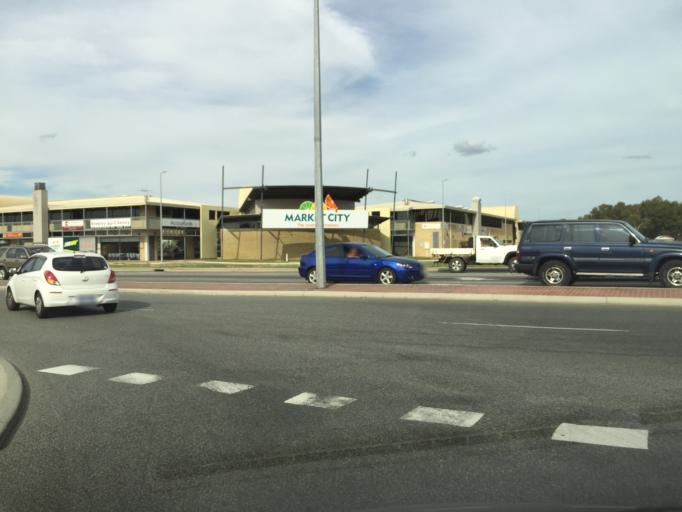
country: AU
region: Western Australia
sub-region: Canning
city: Willetton
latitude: -32.0717
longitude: 115.8930
